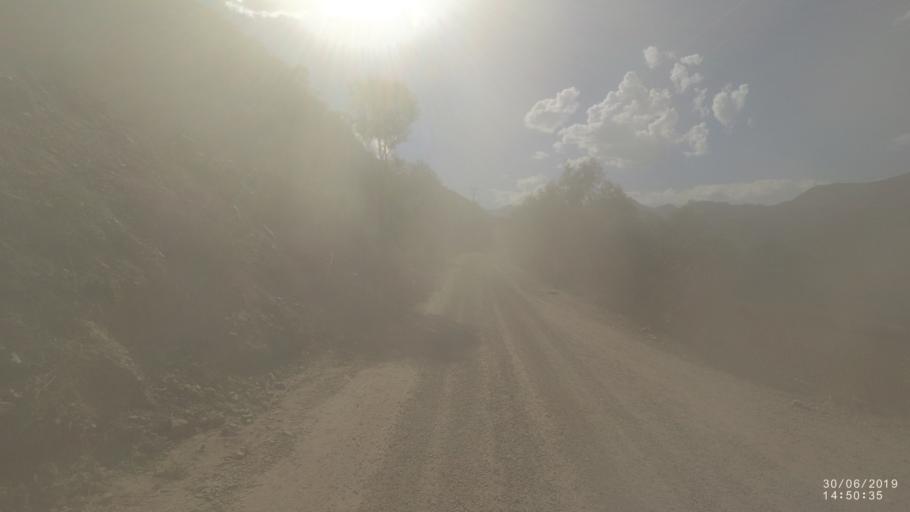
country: BO
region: Cochabamba
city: Irpa Irpa
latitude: -17.7768
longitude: -66.3440
